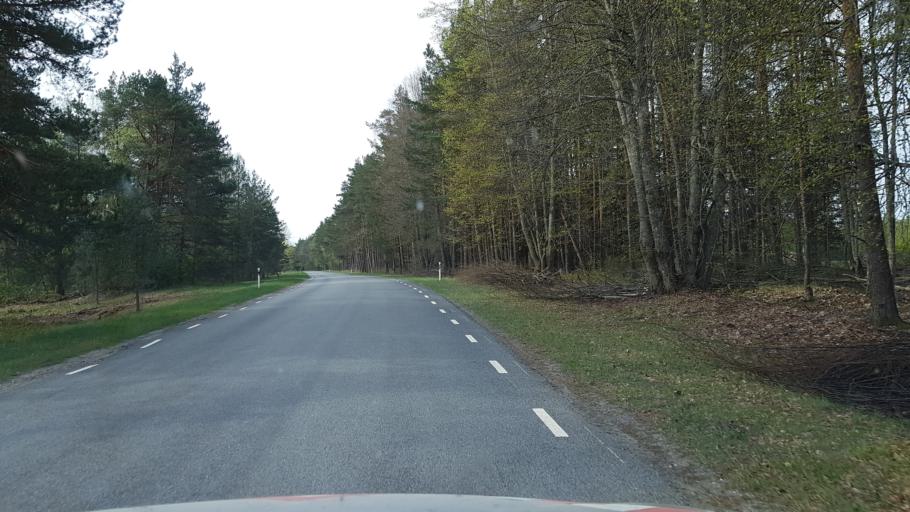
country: EE
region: Paernumaa
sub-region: Audru vald
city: Audru
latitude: 58.3569
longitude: 24.2566
